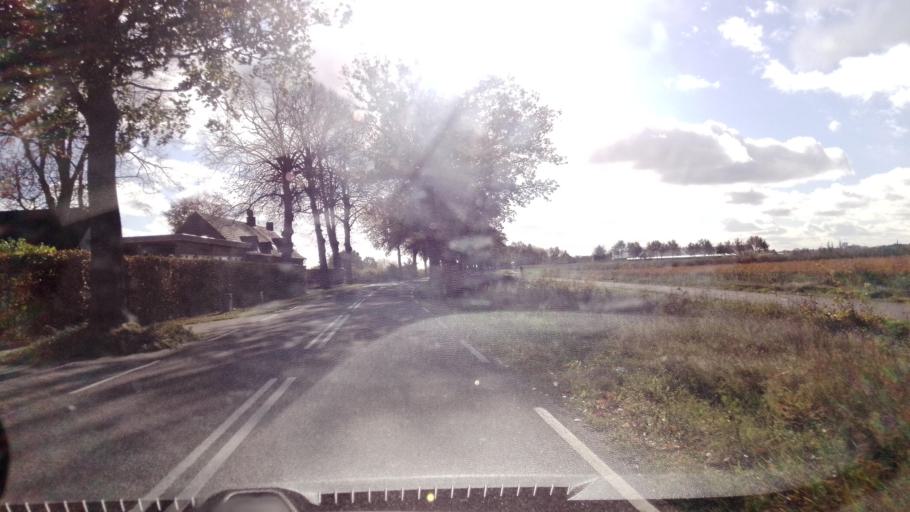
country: NL
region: Limburg
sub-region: Gemeente Venlo
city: Arcen
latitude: 51.4346
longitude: 6.1486
